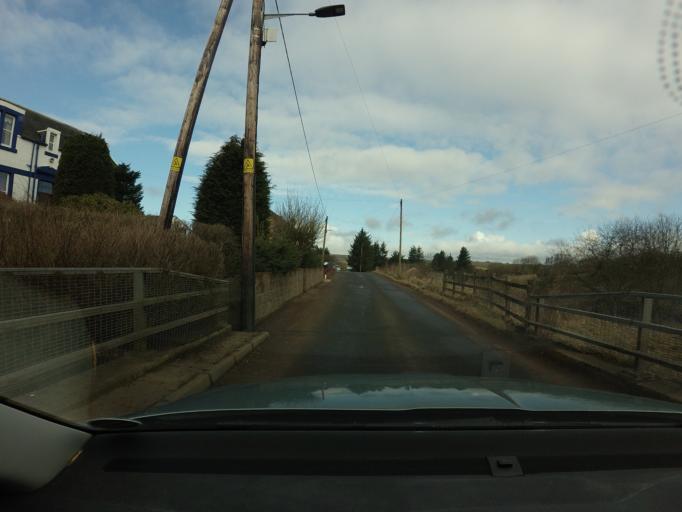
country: GB
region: Scotland
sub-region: South Lanarkshire
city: Lanark
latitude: 55.6063
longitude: -3.7885
